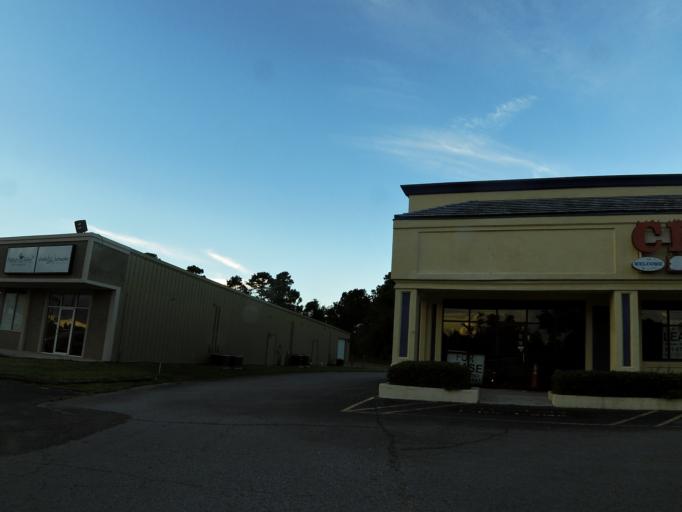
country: US
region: Georgia
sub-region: Camden County
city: St Marys
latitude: 30.7541
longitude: -81.5795
